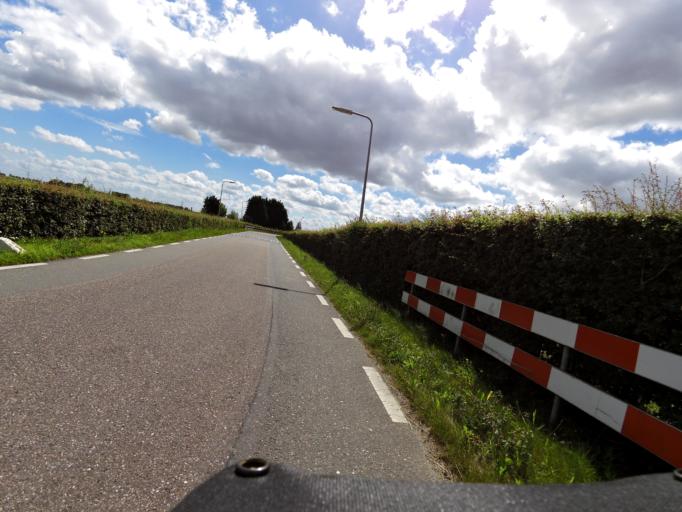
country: NL
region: South Holland
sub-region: Gemeente Oud-Beijerland
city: Oud-Beijerland
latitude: 51.8268
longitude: 4.3699
